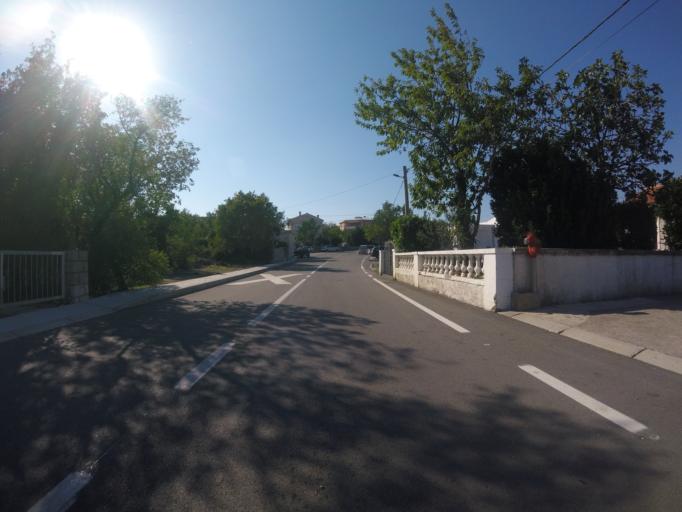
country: HR
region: Primorsko-Goranska
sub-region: Grad Crikvenica
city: Jadranovo
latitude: 45.2269
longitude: 14.6172
